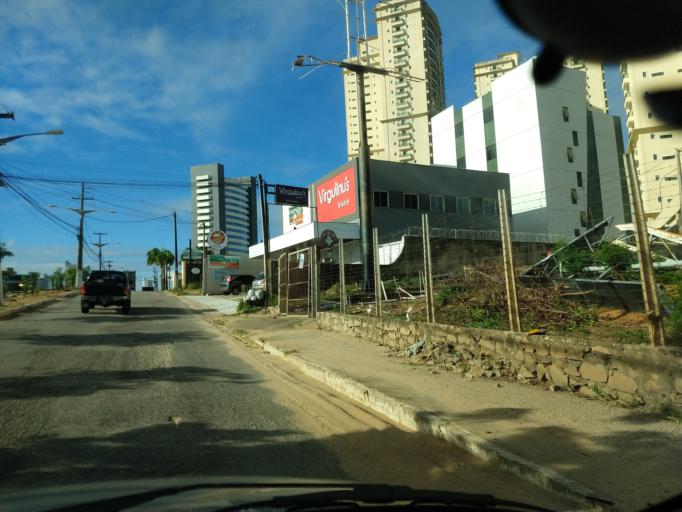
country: BR
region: Rio Grande do Norte
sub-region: Natal
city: Natal
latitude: -5.8365
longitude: -35.2251
